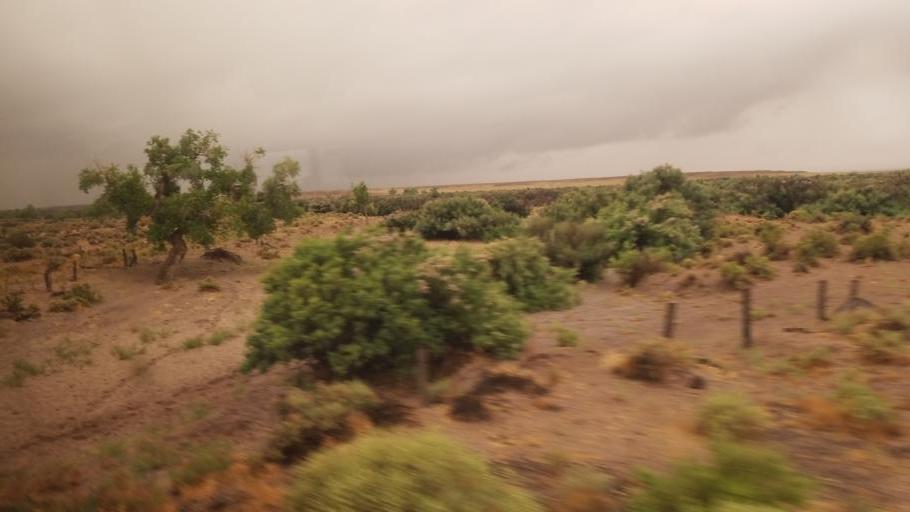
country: US
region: Arizona
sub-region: Navajo County
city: Joseph City
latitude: 34.9639
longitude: -110.4086
